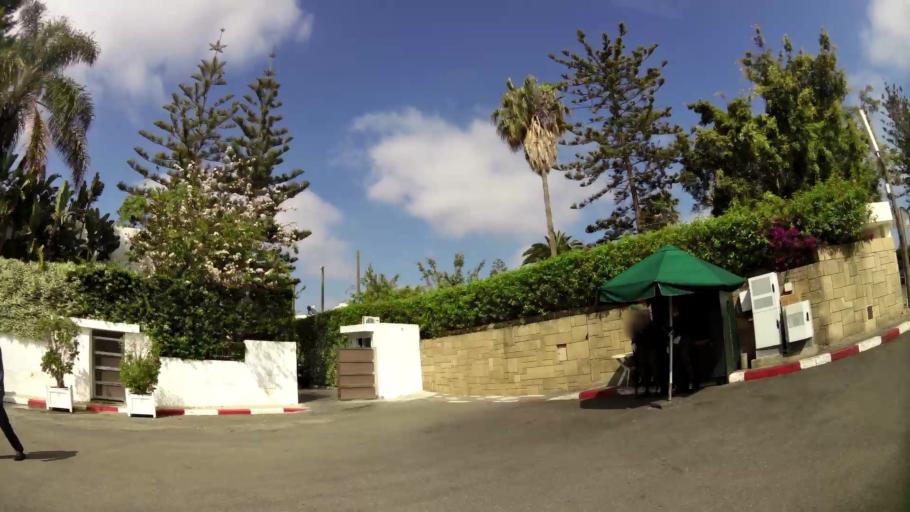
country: MA
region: Rabat-Sale-Zemmour-Zaer
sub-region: Rabat
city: Rabat
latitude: 33.9757
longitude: -6.8415
